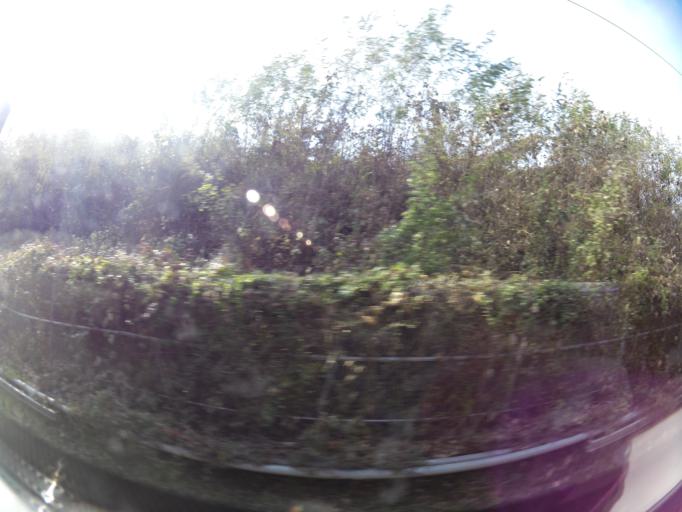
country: KR
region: Daejeon
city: Sintansin
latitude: 36.4663
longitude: 127.4218
